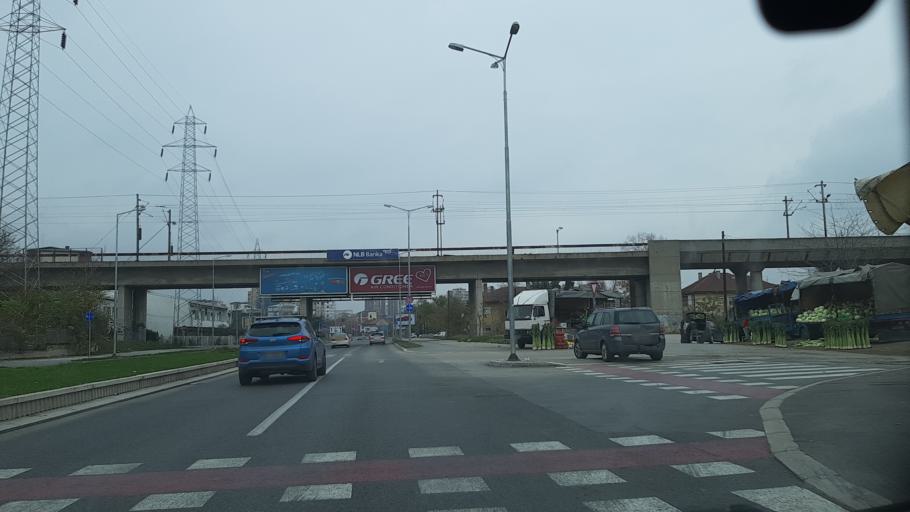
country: MK
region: Karpos
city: Skopje
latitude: 41.9874
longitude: 21.4432
